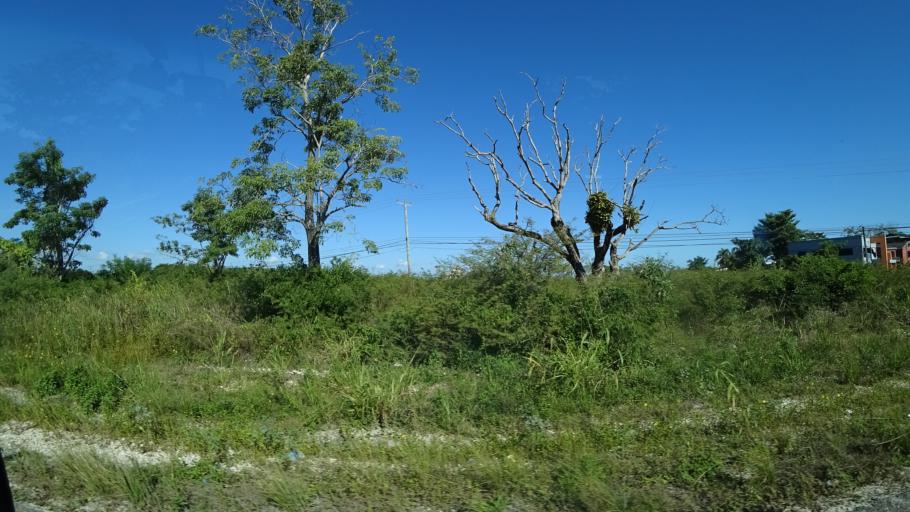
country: BZ
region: Belize
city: Belize City
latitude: 17.5428
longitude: -88.2617
